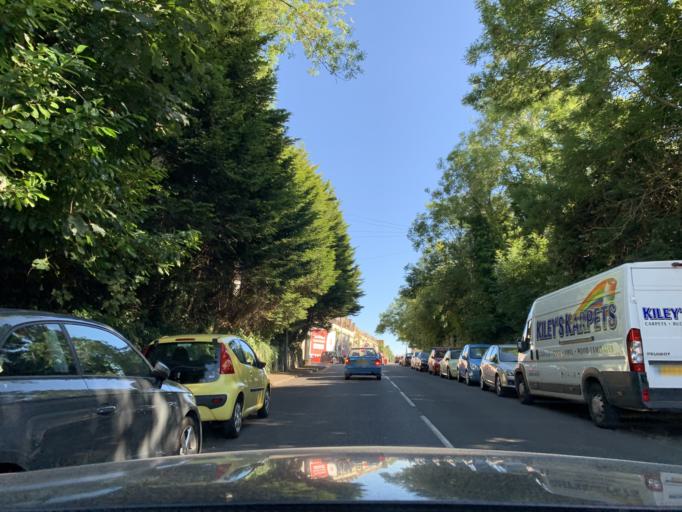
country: GB
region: England
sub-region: East Sussex
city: Saint Leonards-on-Sea
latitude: 50.8703
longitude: 0.5550
